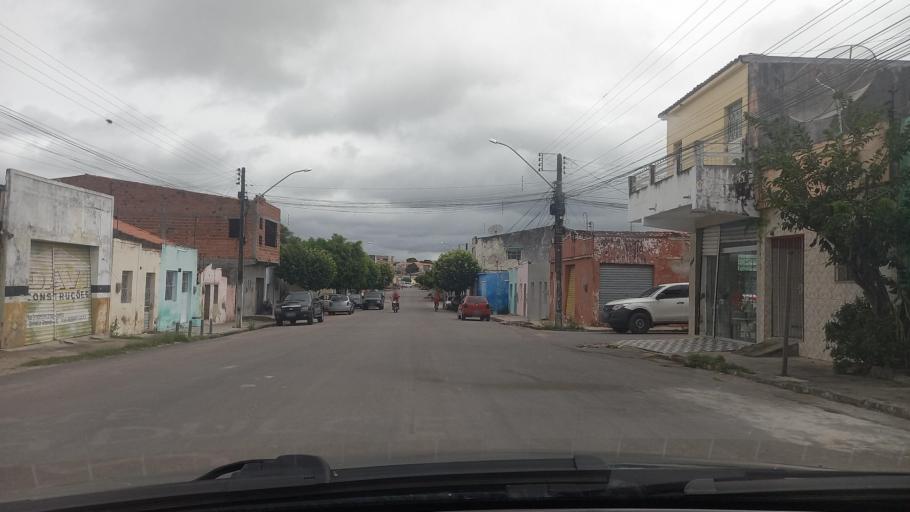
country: BR
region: Alagoas
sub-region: Delmiro Gouveia
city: Delmiro Gouveia
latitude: -9.3842
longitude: -38.0013
